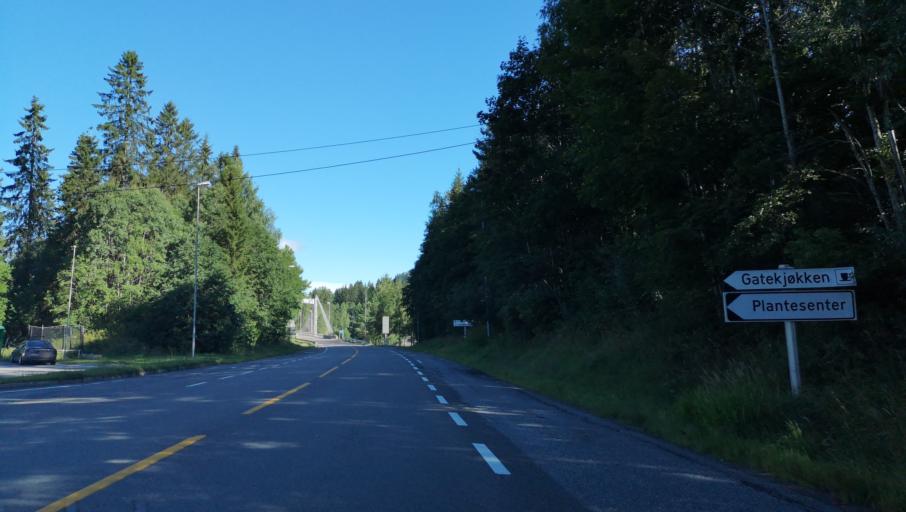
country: NO
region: Ostfold
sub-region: Spydeberg
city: Spydeberg
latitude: 59.6005
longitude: 11.1031
